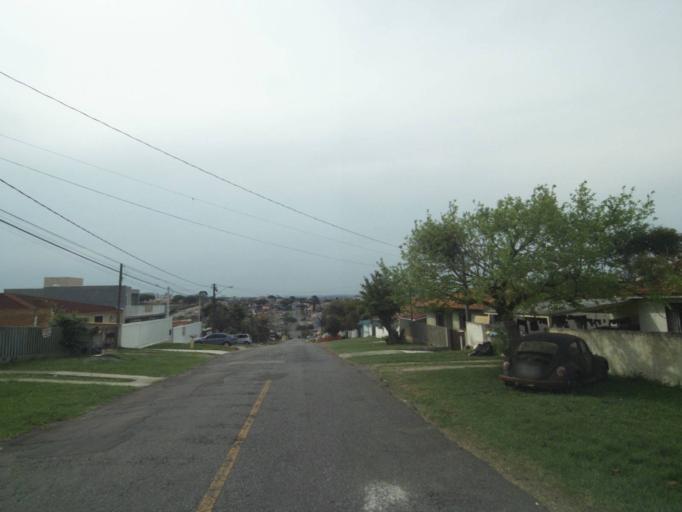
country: BR
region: Parana
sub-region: Pinhais
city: Pinhais
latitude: -25.3989
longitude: -49.1997
